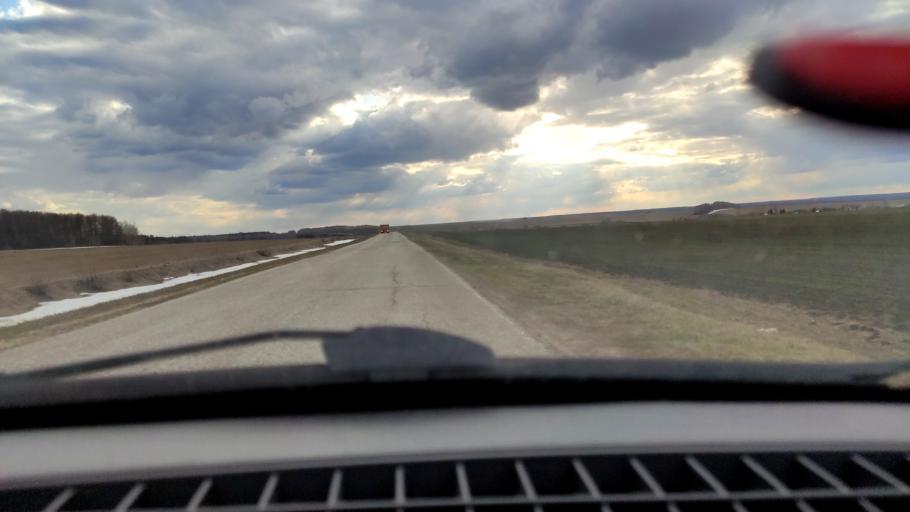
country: RU
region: Bashkortostan
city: Karmaskaly
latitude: 54.3155
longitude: 55.9677
